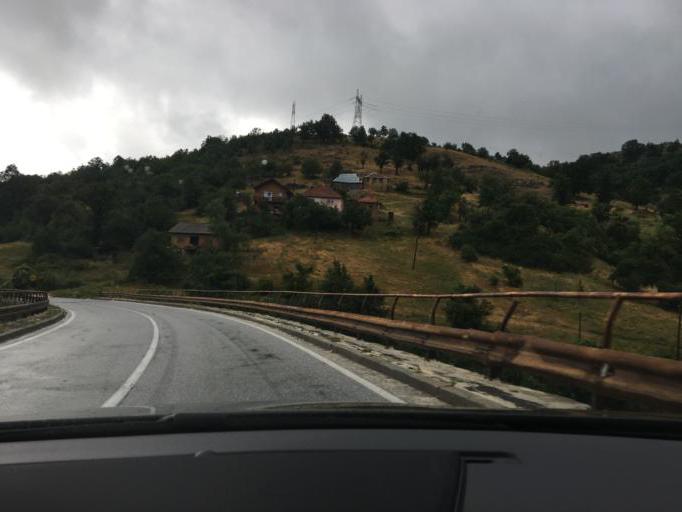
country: MK
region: Kriva Palanka
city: Kriva Palanka
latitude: 42.2218
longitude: 22.4478
